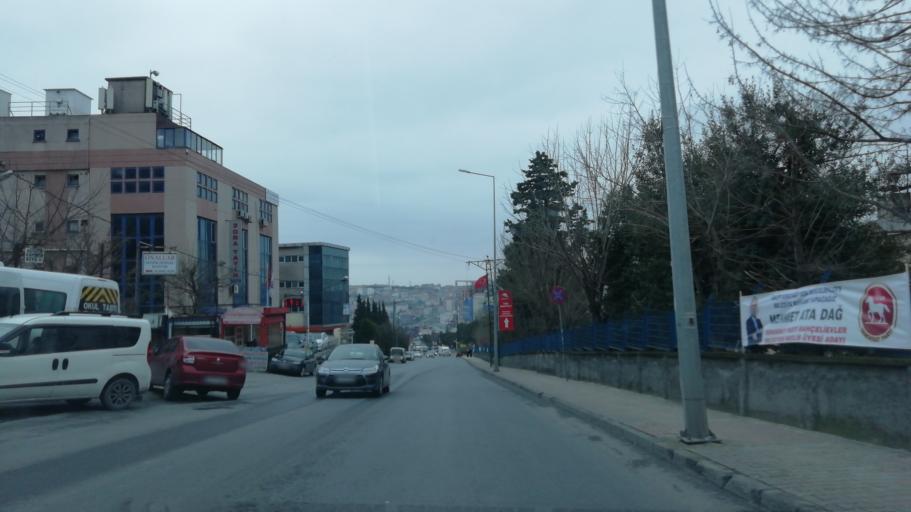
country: TR
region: Istanbul
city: Mahmutbey
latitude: 41.0159
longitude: 28.8213
